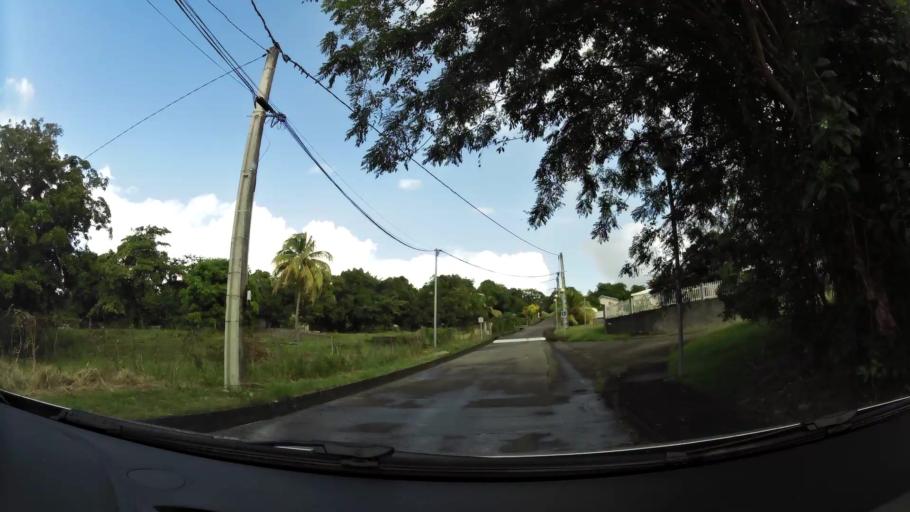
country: MQ
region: Martinique
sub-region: Martinique
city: Sainte-Luce
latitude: 14.5059
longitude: -60.9648
